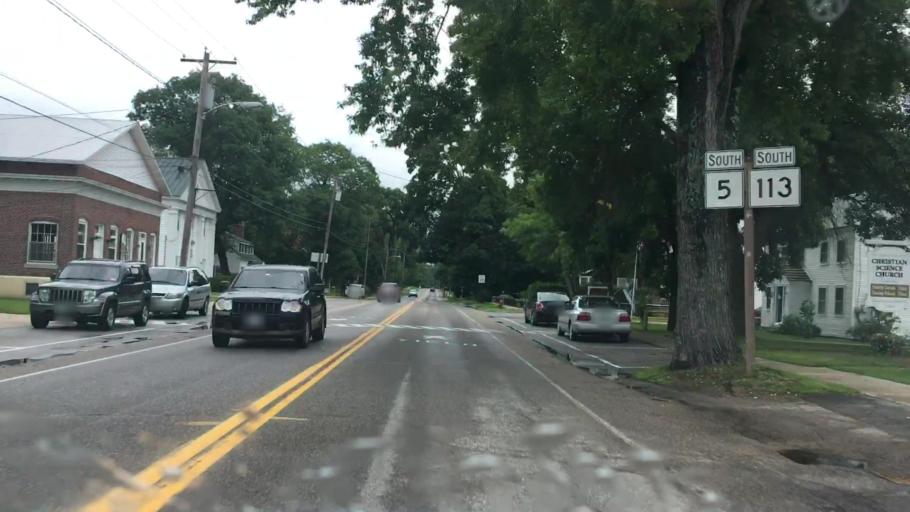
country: US
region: Maine
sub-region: Oxford County
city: Fryeburg
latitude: 44.0162
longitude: -70.9793
